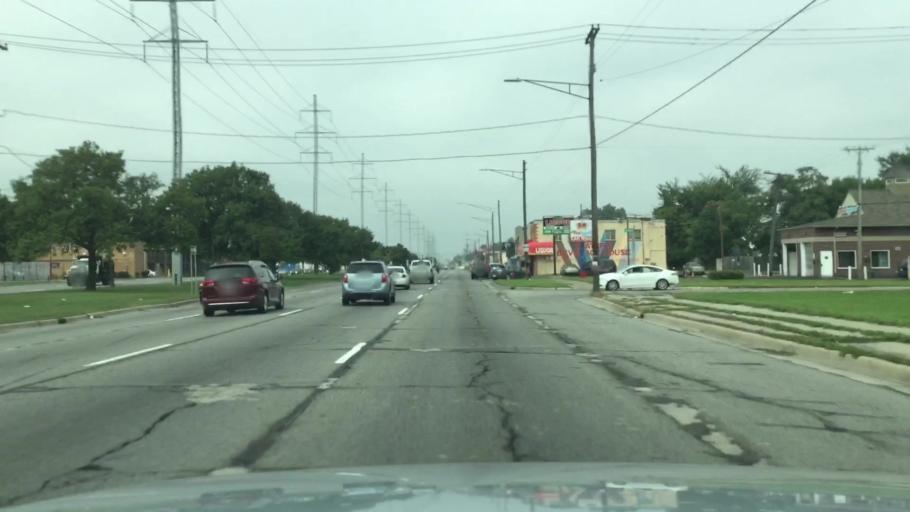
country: US
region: Michigan
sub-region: Macomb County
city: Warren
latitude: 42.4494
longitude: -82.9949
